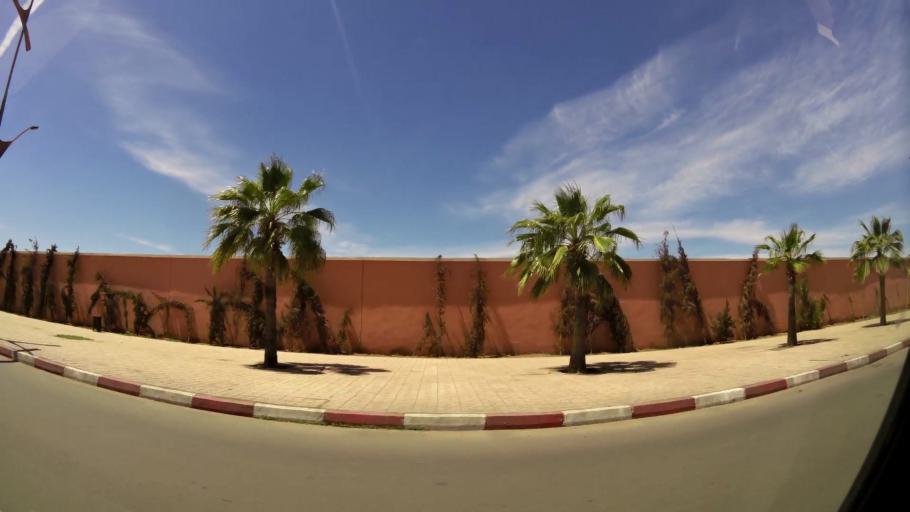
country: MA
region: Marrakech-Tensift-Al Haouz
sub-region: Marrakech
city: Marrakesh
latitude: 31.6158
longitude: -7.9916
